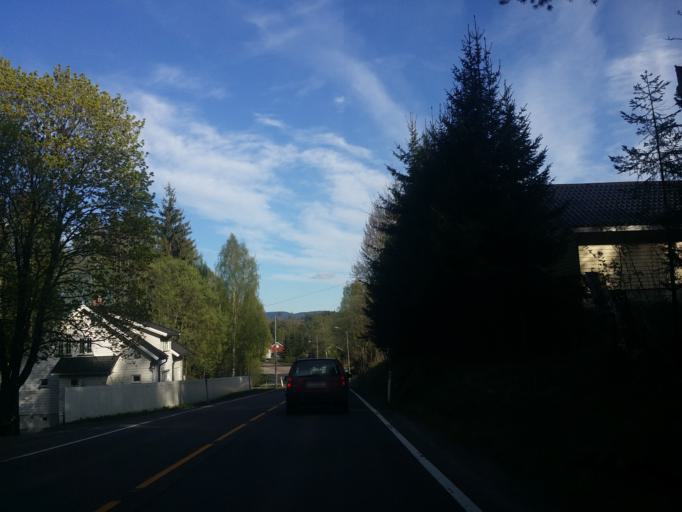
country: NO
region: Buskerud
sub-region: Kongsberg
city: Kongsberg
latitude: 59.6266
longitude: 9.5958
